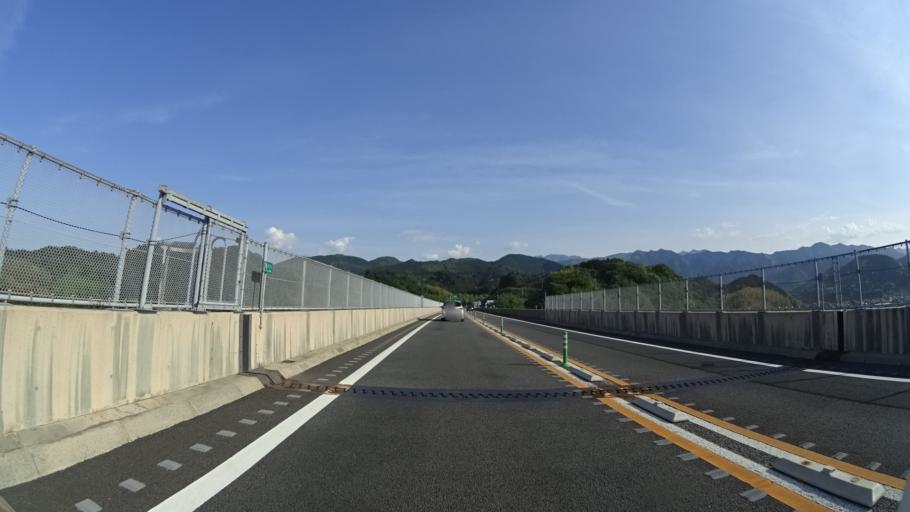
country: JP
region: Ehime
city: Saijo
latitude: 33.8891
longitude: 133.0863
